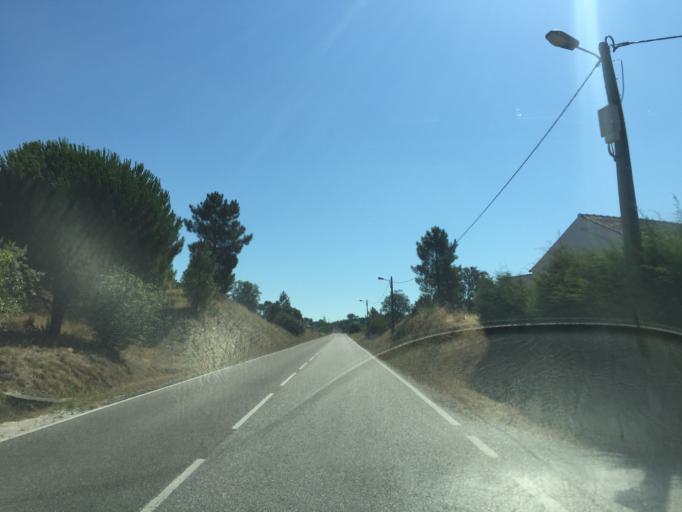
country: PT
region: Santarem
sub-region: Constancia
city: Constancia
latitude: 39.5379
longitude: -8.3062
